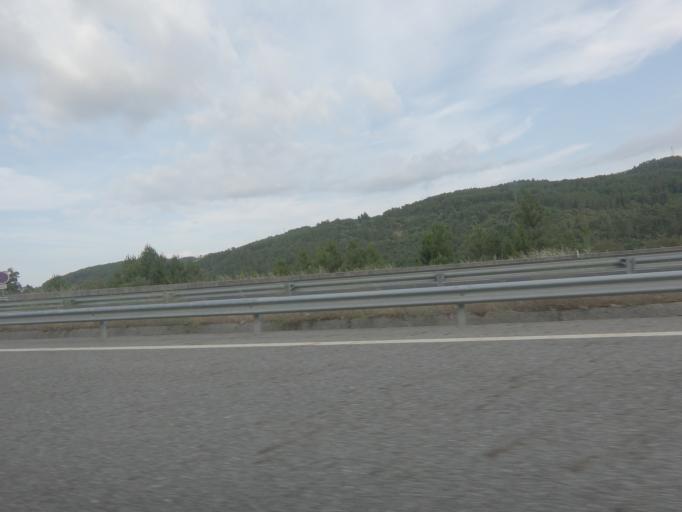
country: PT
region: Vila Real
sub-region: Boticas
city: Boticas
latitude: 41.6838
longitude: -7.5651
